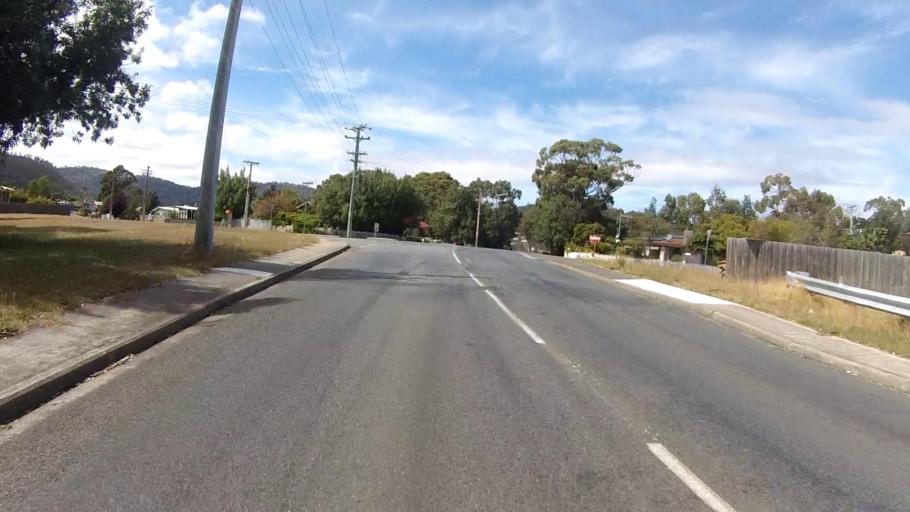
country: AU
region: Tasmania
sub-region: Clarence
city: Lindisfarne
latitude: -42.8092
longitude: 147.3504
